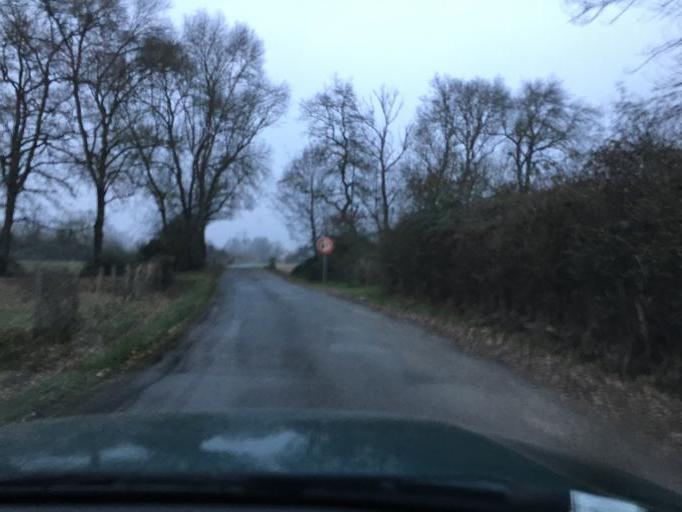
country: FR
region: Centre
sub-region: Departement du Loiret
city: Lailly-en-Val
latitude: 47.7615
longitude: 1.6672
